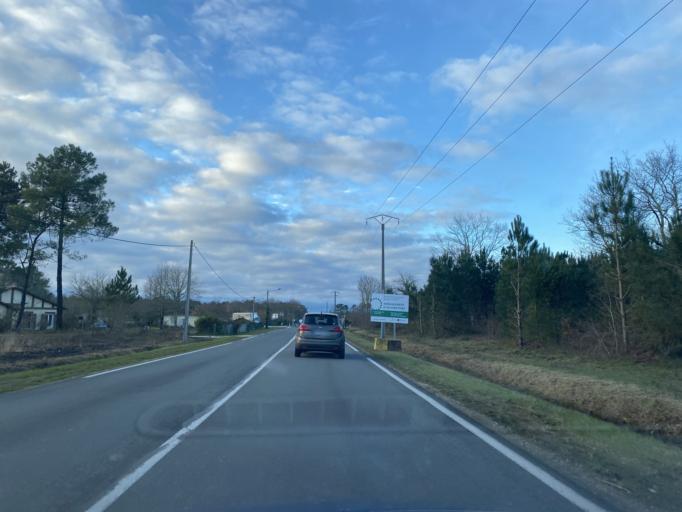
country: FR
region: Aquitaine
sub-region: Departement de la Gironde
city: Marcheprime
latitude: 44.7174
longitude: -0.8803
